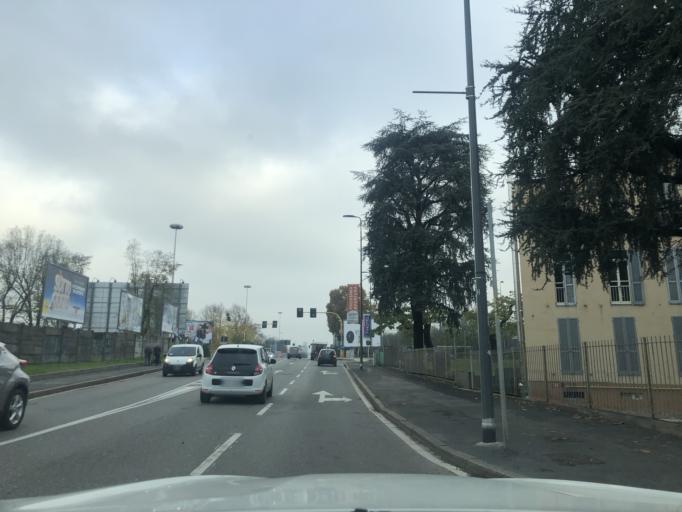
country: IT
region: Lombardy
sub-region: Citta metropolitana di Milano
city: Baranzate
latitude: 45.4867
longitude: 9.1302
